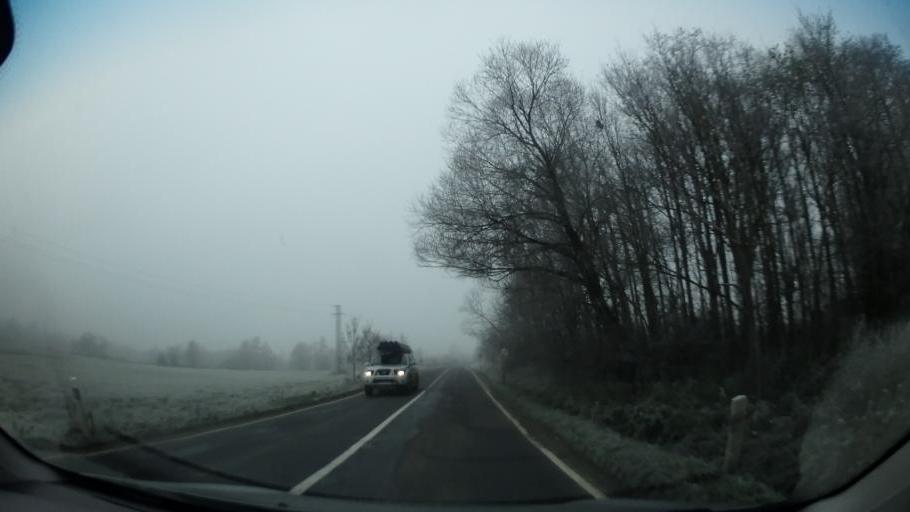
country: CZ
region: Vysocina
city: Budisov
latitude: 49.2662
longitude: 15.9351
